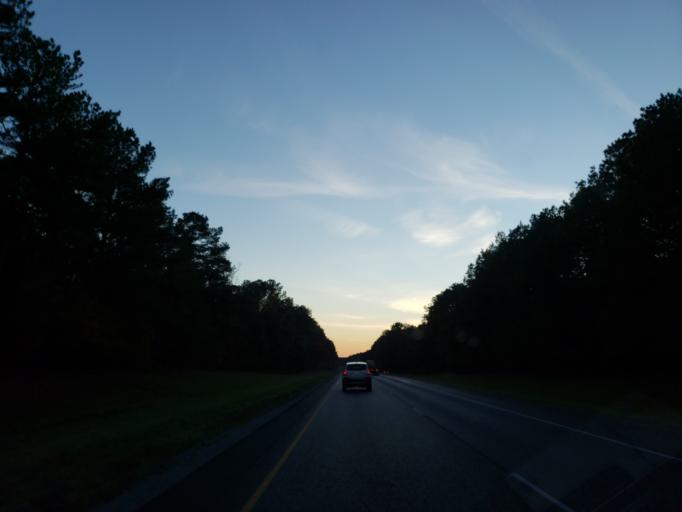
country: US
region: Alabama
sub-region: Sumter County
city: York
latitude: 32.5462
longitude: -88.2754
